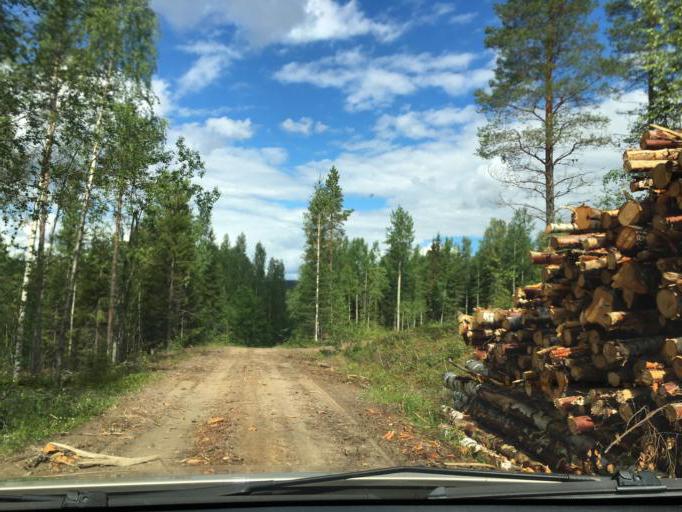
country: SE
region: Norrbotten
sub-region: Overkalix Kommun
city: OEverkalix
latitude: 66.1505
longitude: 22.7968
